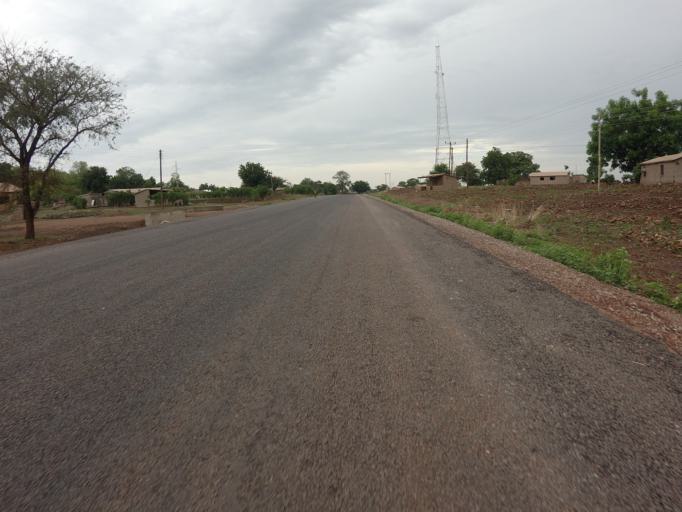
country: GH
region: Upper East
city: Bolgatanga
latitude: 10.8472
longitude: -0.6816
